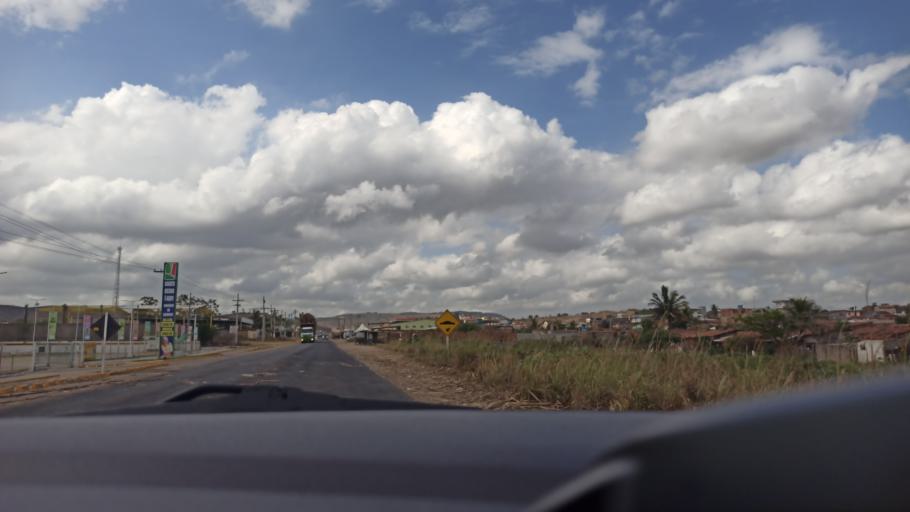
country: BR
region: Pernambuco
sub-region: Timbauba
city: Timbauba
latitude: -7.4930
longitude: -35.2970
